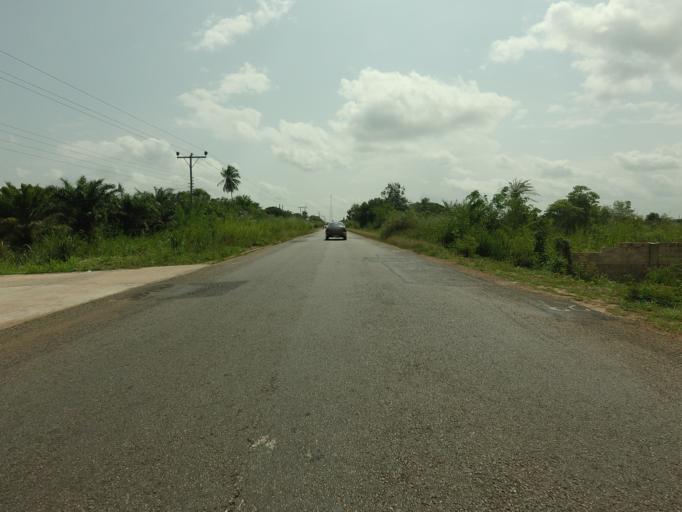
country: TG
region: Maritime
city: Lome
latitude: 6.2295
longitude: 1.0110
